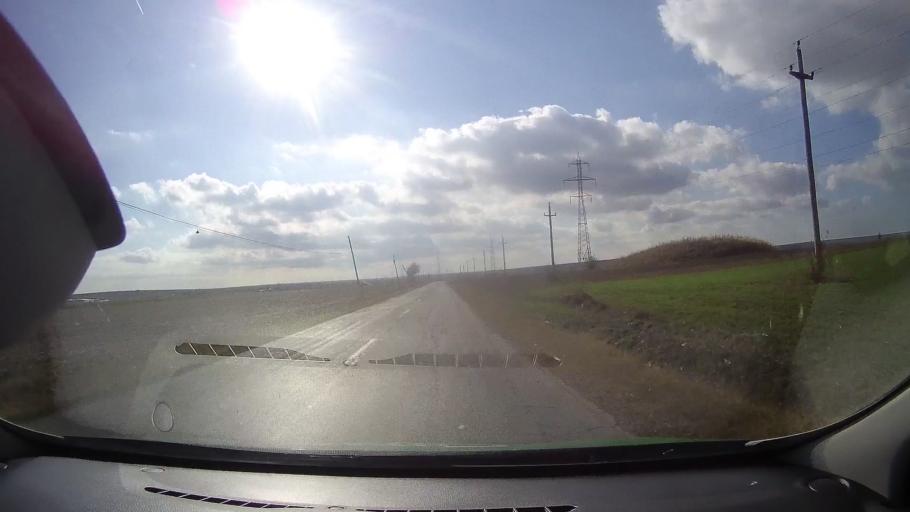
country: RO
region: Constanta
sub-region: Comuna Istria
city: Nuntasi
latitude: 44.5366
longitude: 28.6872
